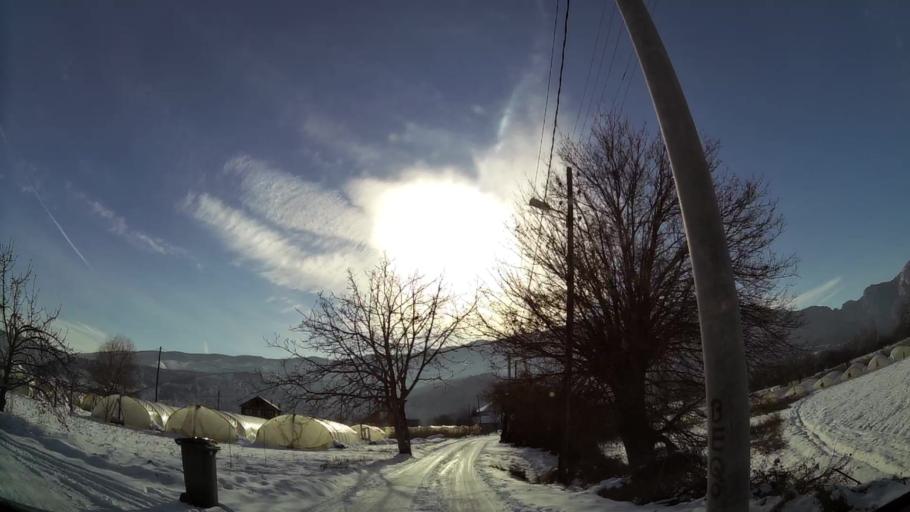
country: MK
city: Grchec
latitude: 41.9888
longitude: 21.3258
